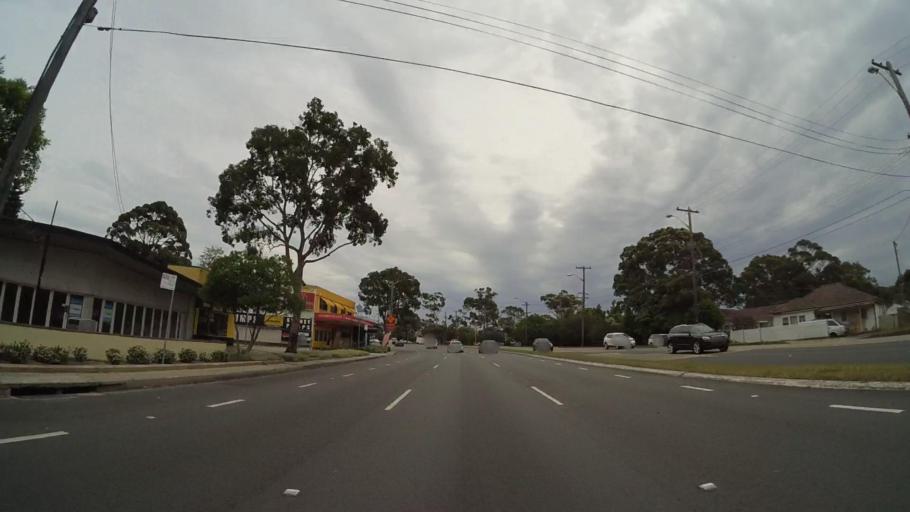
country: AU
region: New South Wales
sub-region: Sutherland Shire
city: Kareela
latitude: -34.0111
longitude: 151.0948
